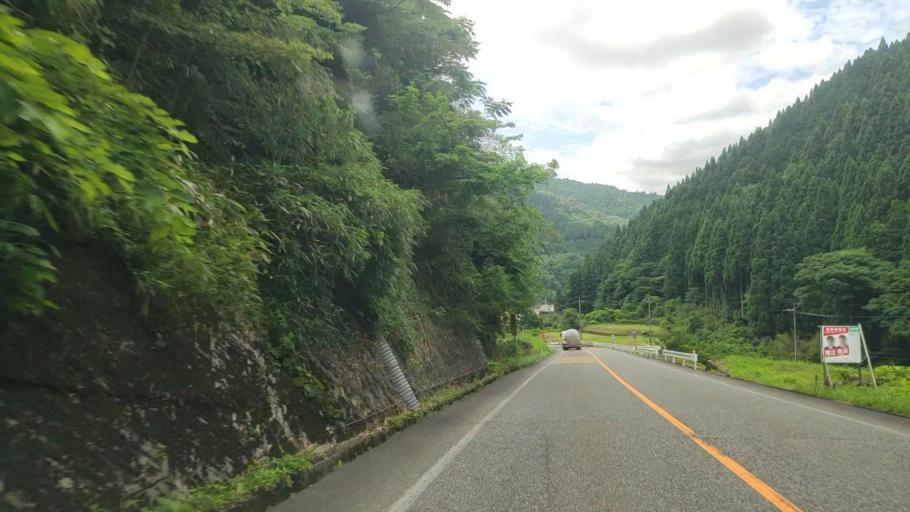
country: JP
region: Tottori
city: Yonago
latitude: 35.2491
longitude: 133.4425
